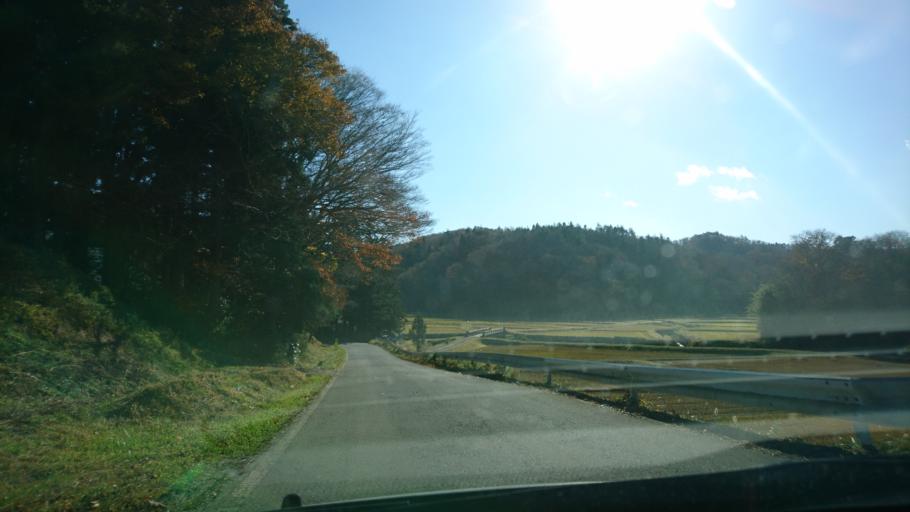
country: JP
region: Iwate
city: Ichinoseki
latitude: 38.9998
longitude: 141.0856
